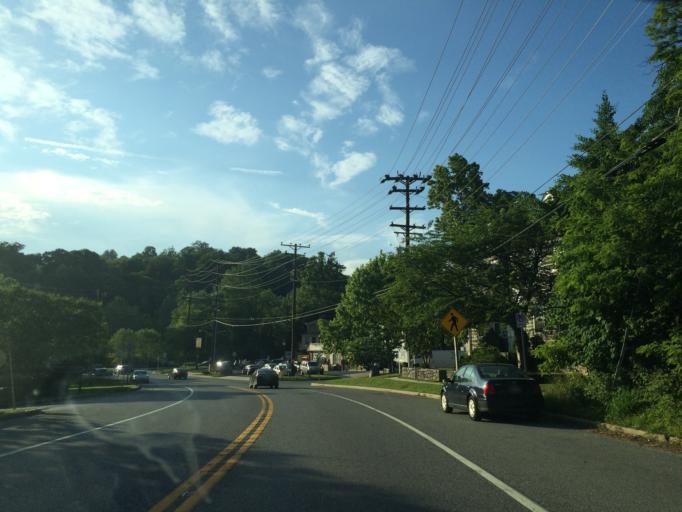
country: US
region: Maryland
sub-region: Howard County
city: Ellicott City
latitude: 39.2669
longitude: -76.7927
